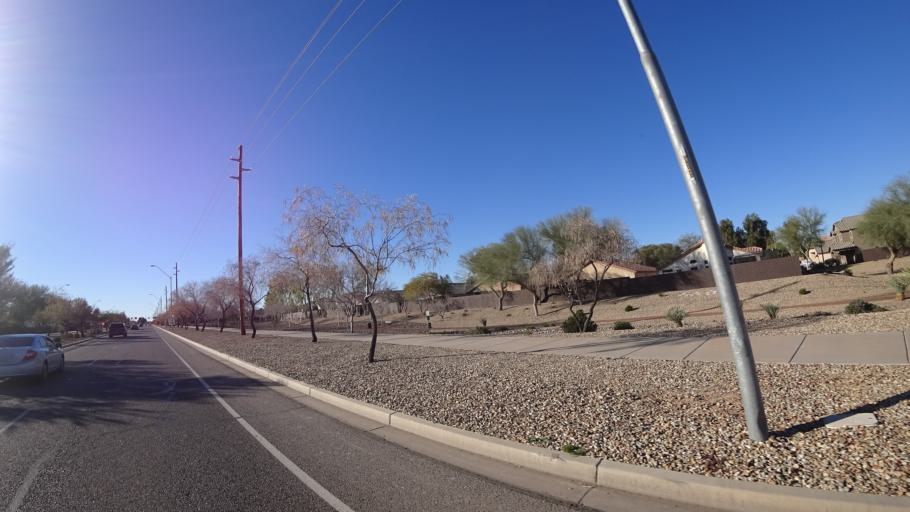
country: US
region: Arizona
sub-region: Maricopa County
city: Goodyear
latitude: 33.4502
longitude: -112.4144
